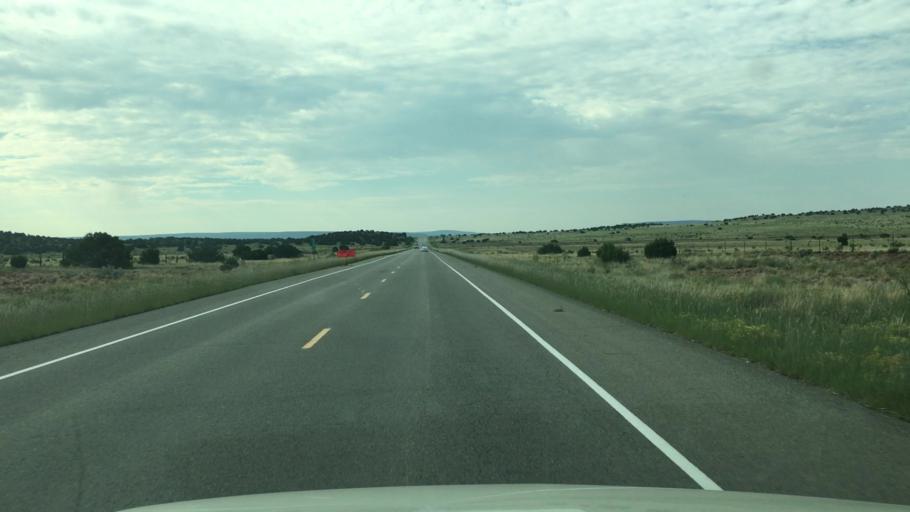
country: US
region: New Mexico
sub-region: Santa Fe County
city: Eldorado at Santa Fe
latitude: 35.4412
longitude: -105.8852
